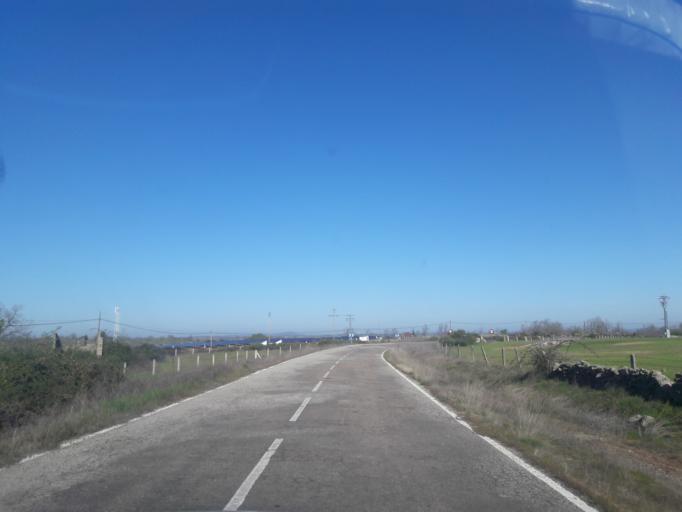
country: ES
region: Castille and Leon
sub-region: Provincia de Salamanca
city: Cabeza del Caballo
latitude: 41.1347
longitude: -6.5562
